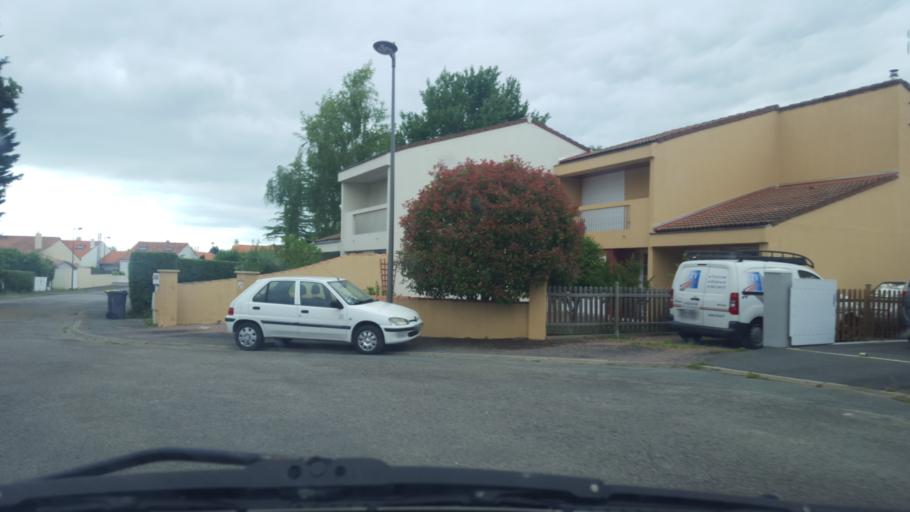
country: FR
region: Pays de la Loire
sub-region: Departement de la Loire-Atlantique
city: Saint-Philbert-de-Grand-Lieu
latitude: 47.0306
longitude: -1.6451
